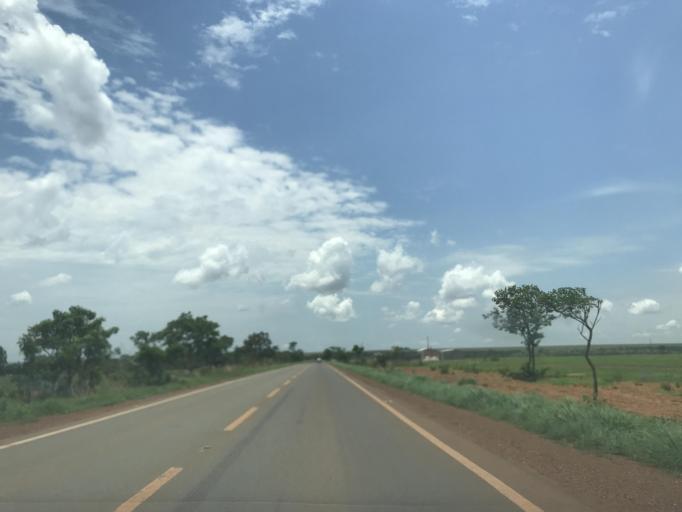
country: BR
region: Goias
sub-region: Luziania
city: Luziania
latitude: -16.4716
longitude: -48.2125
